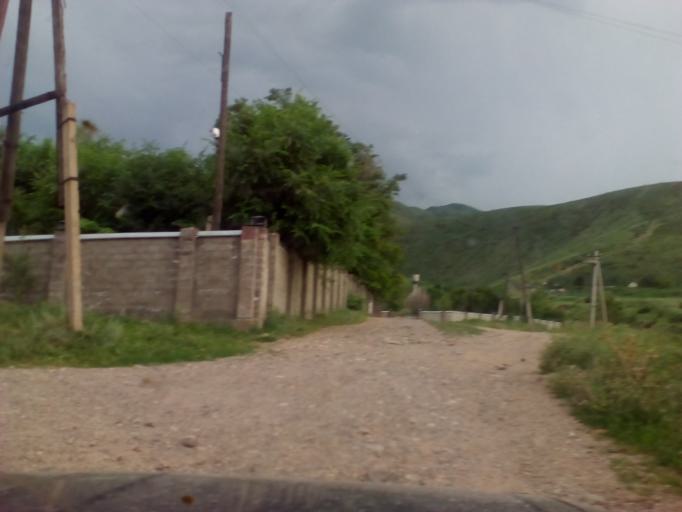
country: KZ
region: Almaty Oblysy
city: Burunday
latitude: 43.1569
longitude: 76.4020
